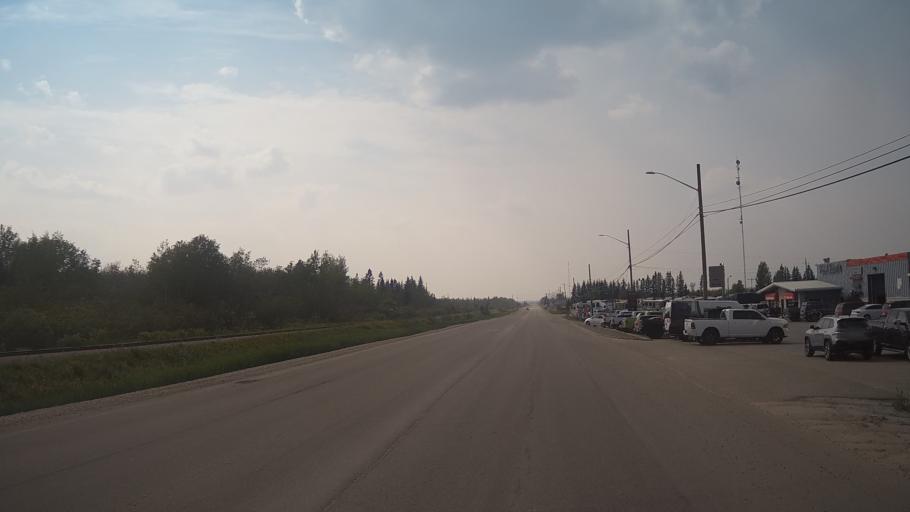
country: CA
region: Ontario
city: Kapuskasing
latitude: 49.3974
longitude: -82.3714
